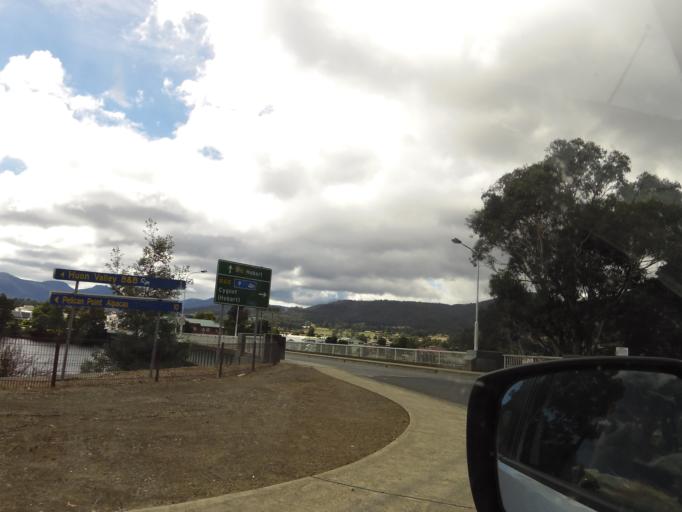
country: AU
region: Tasmania
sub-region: Huon Valley
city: Huonville
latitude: -43.0347
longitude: 147.0458
